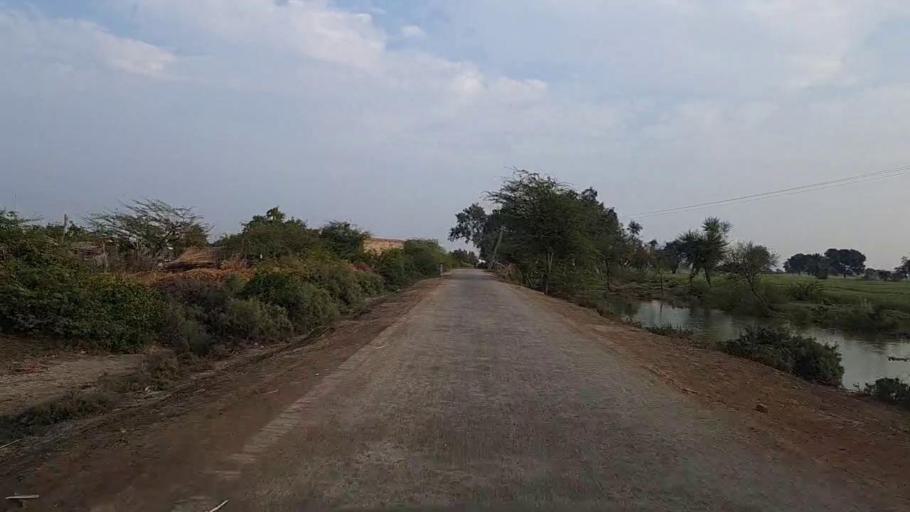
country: PK
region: Sindh
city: Pithoro
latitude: 25.4531
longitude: 69.2834
